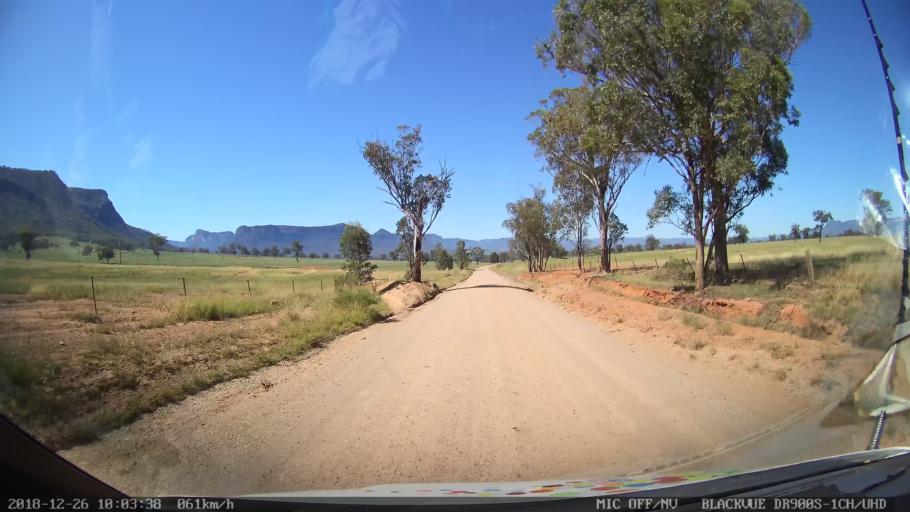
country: AU
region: New South Wales
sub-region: Mid-Western Regional
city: Kandos
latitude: -33.0633
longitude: 150.2173
